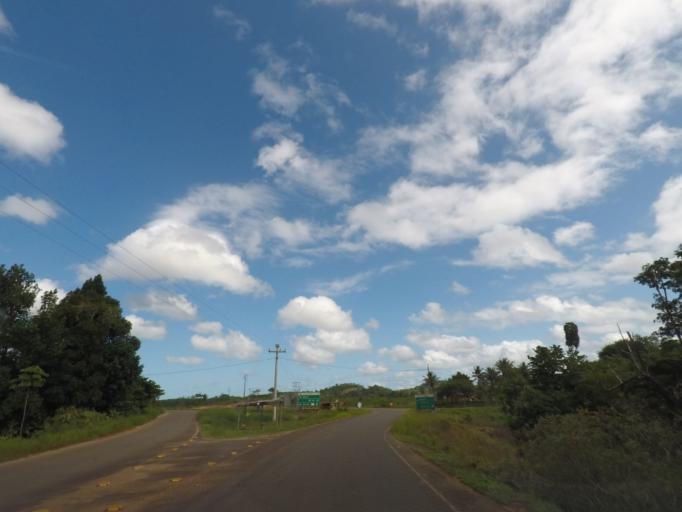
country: BR
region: Bahia
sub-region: Itacare
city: Itacare
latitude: -14.2270
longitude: -39.0945
